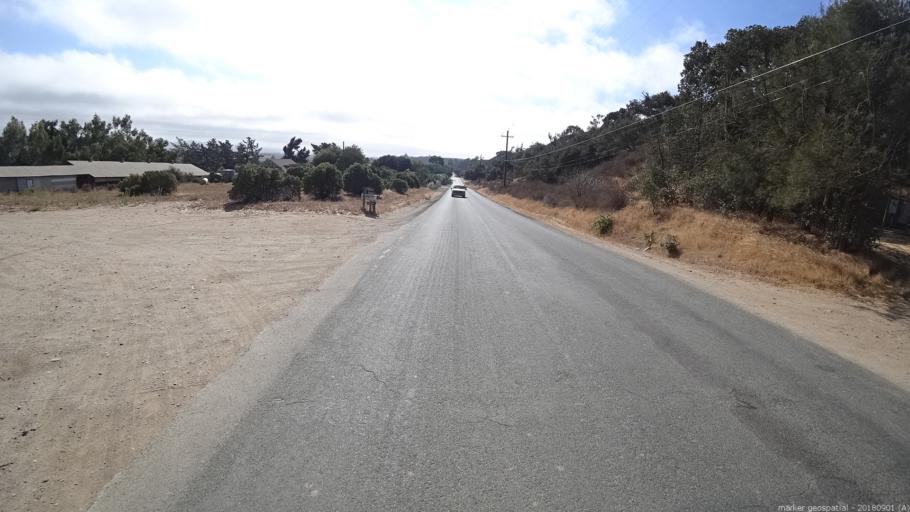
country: US
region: California
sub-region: Monterey County
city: Soledad
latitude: 36.3893
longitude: -121.3647
